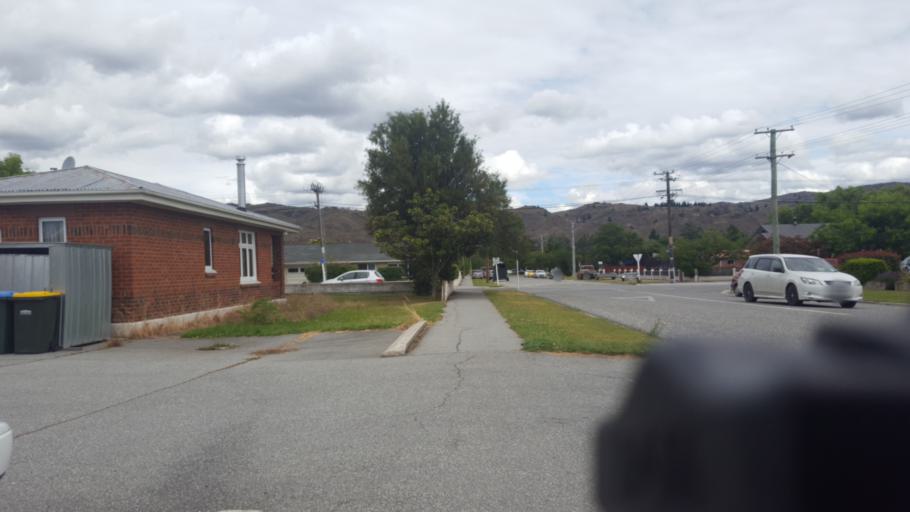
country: NZ
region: Otago
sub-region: Queenstown-Lakes District
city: Wanaka
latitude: -45.2537
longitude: 169.3888
